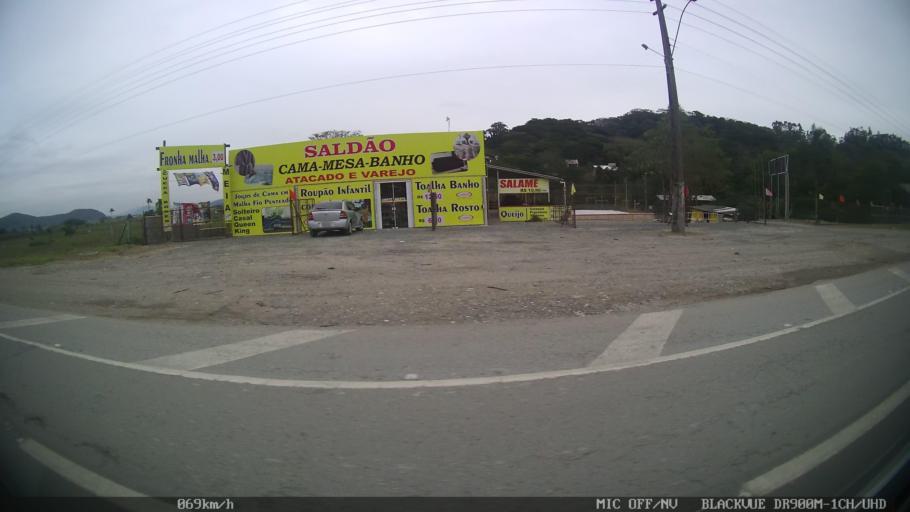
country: BR
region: Santa Catarina
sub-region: Penha
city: Penha
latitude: -26.8012
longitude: -48.6803
